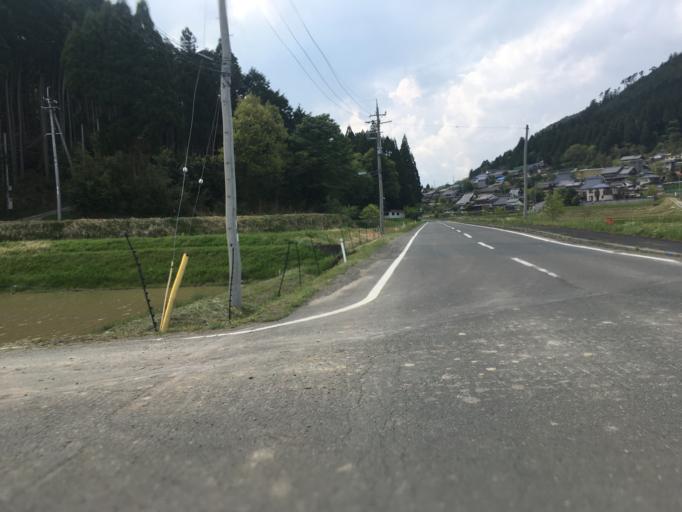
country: JP
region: Kyoto
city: Kameoka
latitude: 35.1069
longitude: 135.5820
